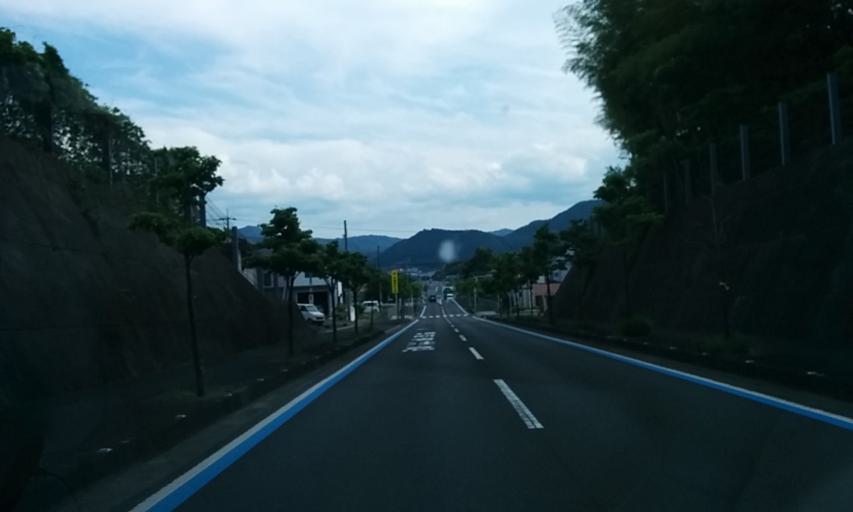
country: JP
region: Kyoto
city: Ayabe
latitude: 35.3159
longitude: 135.2603
